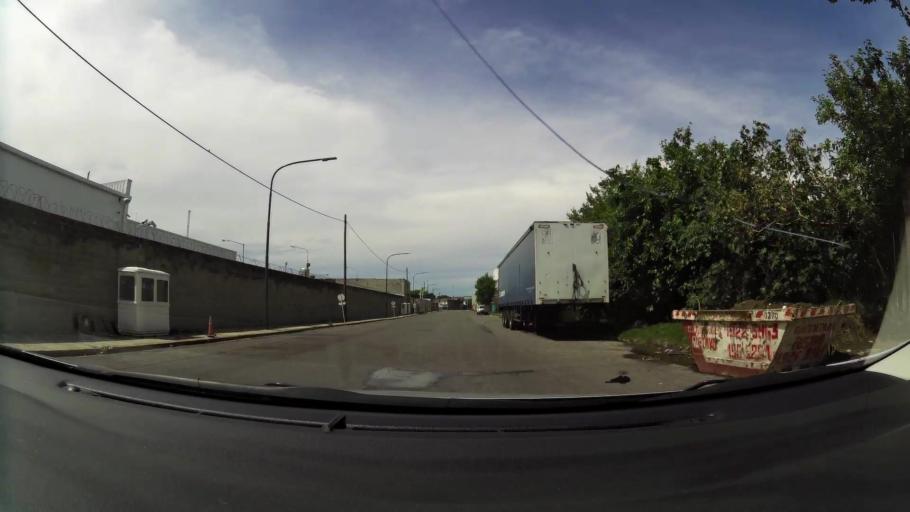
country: AR
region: Buenos Aires F.D.
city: Villa Lugano
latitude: -34.6665
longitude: -58.4370
